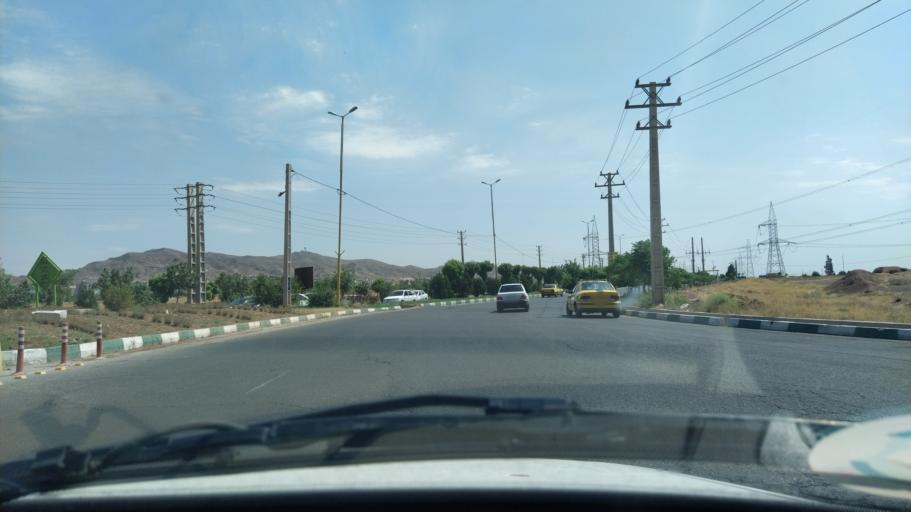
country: IR
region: Tehran
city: Robat Karim
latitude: 35.4617
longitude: 50.9666
